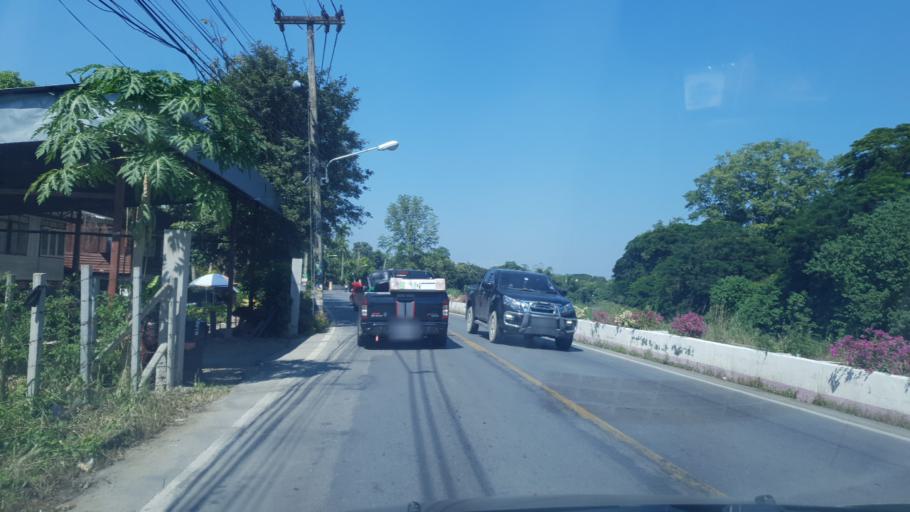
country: TH
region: Chiang Mai
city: Saraphi
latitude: 18.7281
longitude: 98.9852
